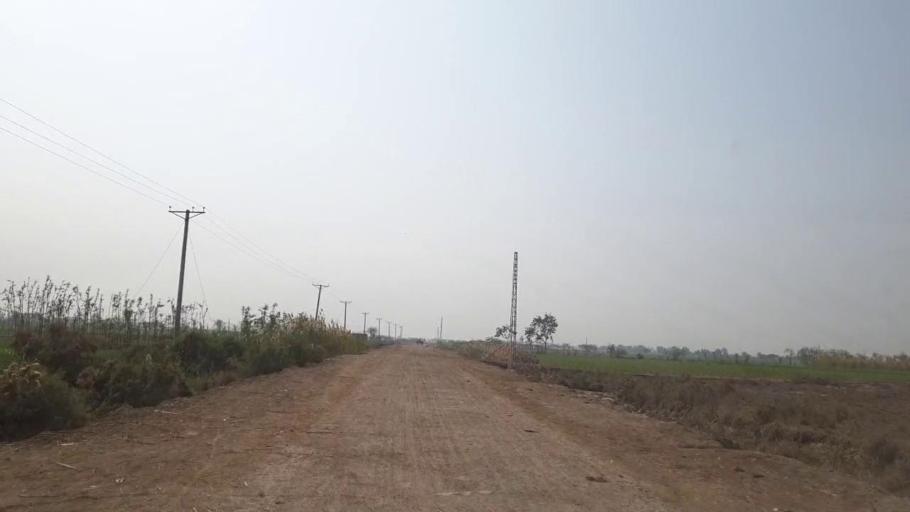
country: PK
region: Sindh
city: Mirpur Khas
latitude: 25.5445
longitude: 69.0688
